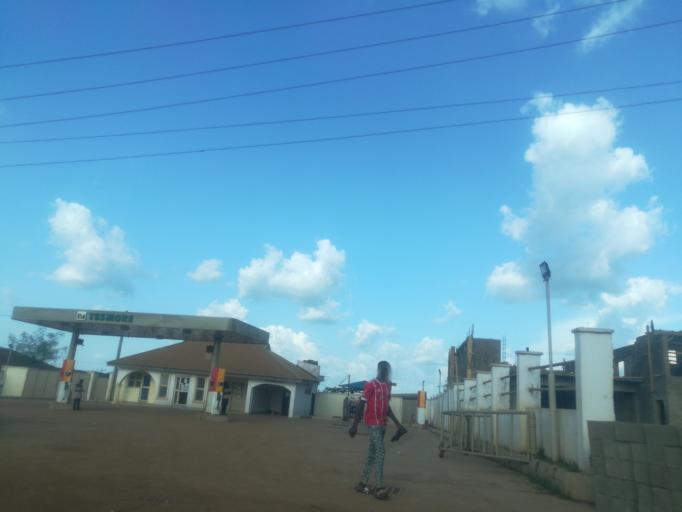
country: NG
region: Oyo
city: Egbeda
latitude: 7.4324
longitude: 3.9835
